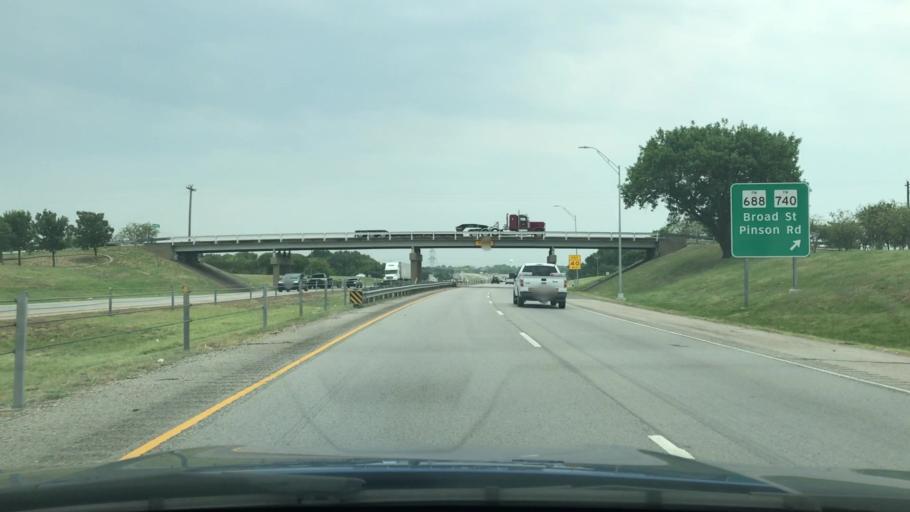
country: US
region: Texas
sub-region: Kaufman County
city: Forney
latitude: 32.7704
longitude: -96.4895
